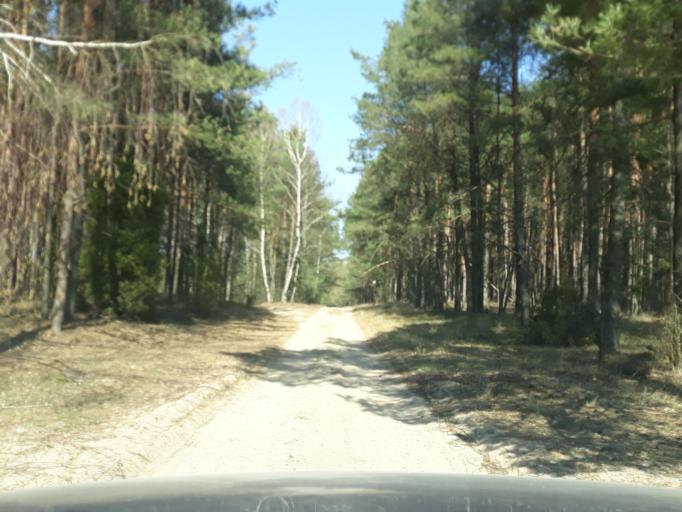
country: PL
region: Pomeranian Voivodeship
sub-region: Powiat bytowski
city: Lipnica
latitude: 53.8514
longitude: 17.4311
